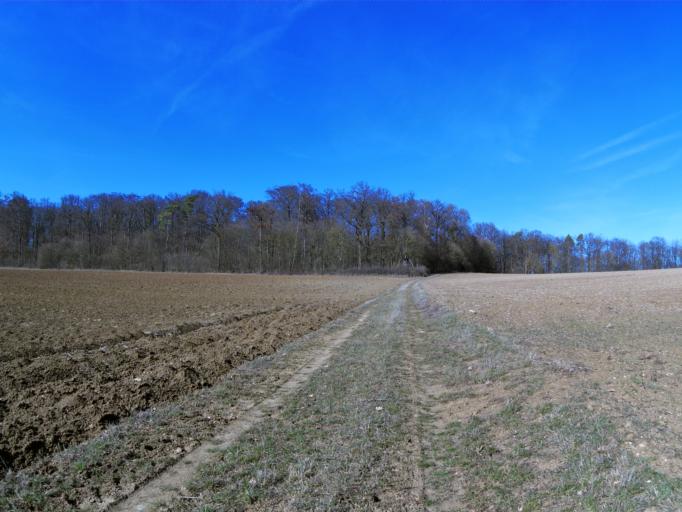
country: DE
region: Bavaria
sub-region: Regierungsbezirk Unterfranken
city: Estenfeld
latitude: 49.8514
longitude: 9.9975
